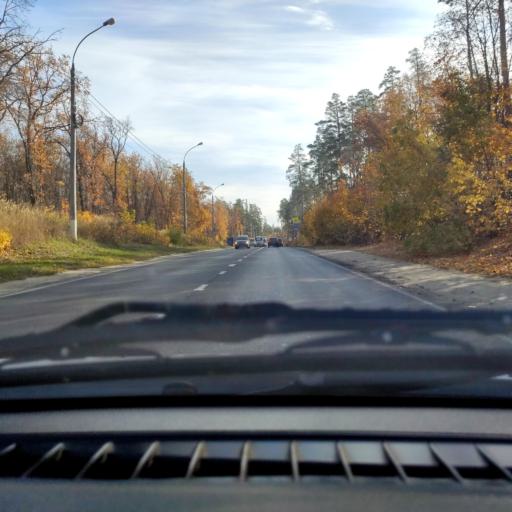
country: RU
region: Samara
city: Tol'yatti
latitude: 53.4929
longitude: 49.2984
